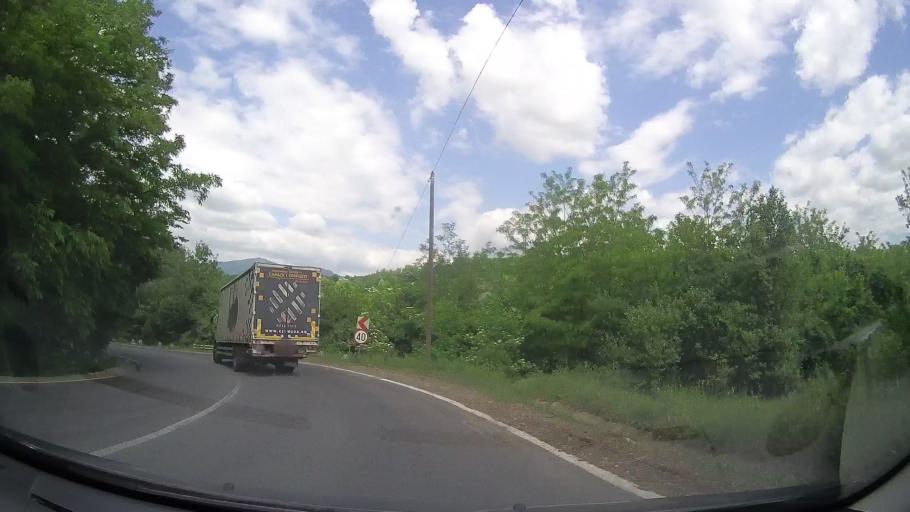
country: RO
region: Prahova
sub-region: Comuna Izvoarele
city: Homoraciu
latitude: 45.2727
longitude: 26.0153
